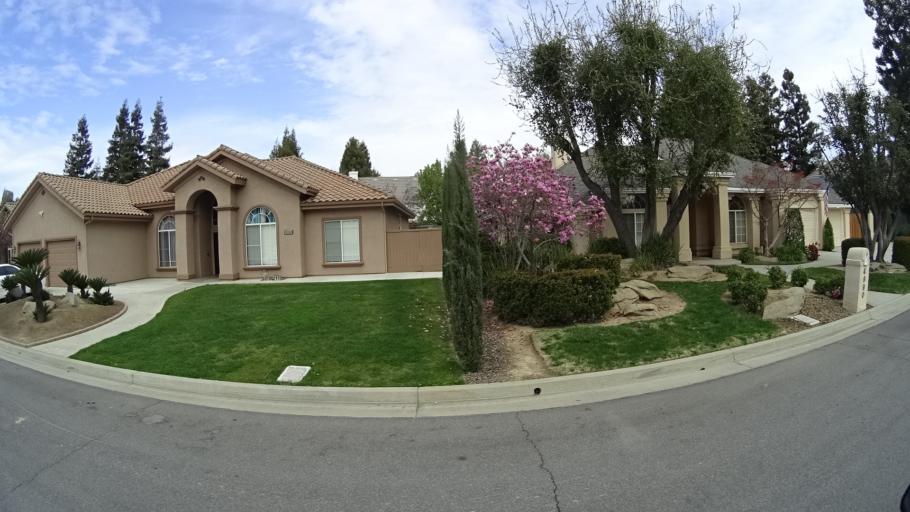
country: US
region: California
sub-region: Fresno County
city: West Park
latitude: 36.8400
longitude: -119.8821
